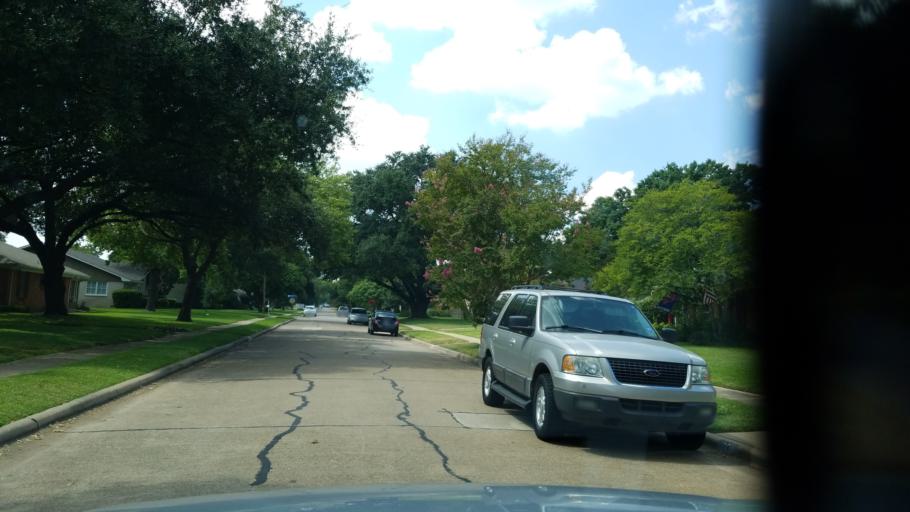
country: US
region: Texas
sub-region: Dallas County
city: Richardson
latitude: 32.9699
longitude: -96.7595
